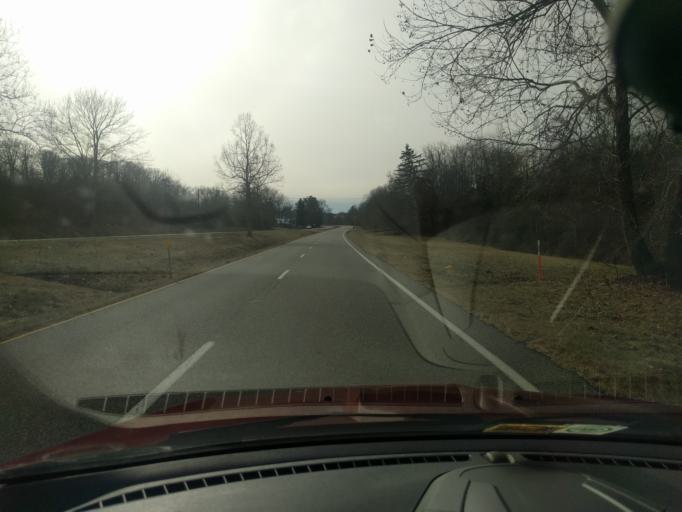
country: US
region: Virginia
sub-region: Augusta County
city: Stuarts Draft
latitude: 37.9360
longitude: -79.1930
